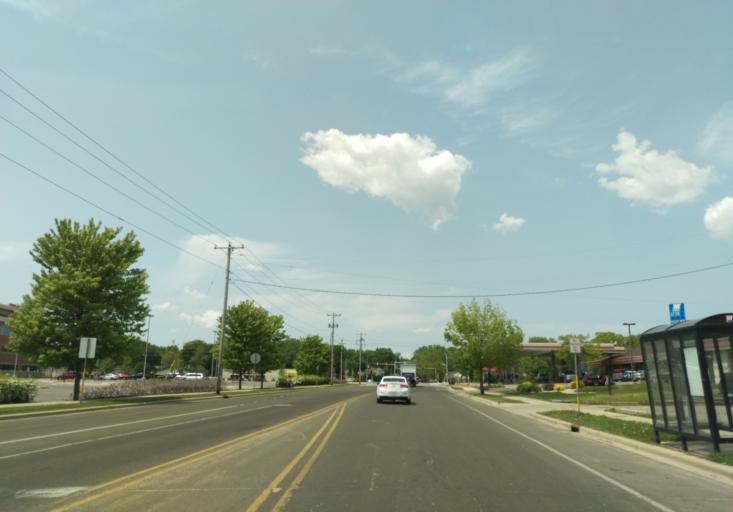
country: US
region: Wisconsin
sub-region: Dane County
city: Monona
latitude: 43.0731
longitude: -89.3070
